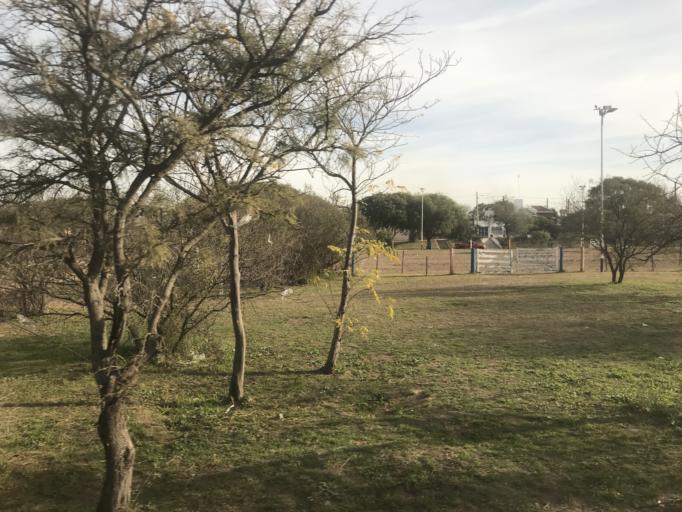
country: AR
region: Cordoba
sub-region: Departamento de Rio Segundo
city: Rio Segundo
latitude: -31.6551
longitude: -63.9093
